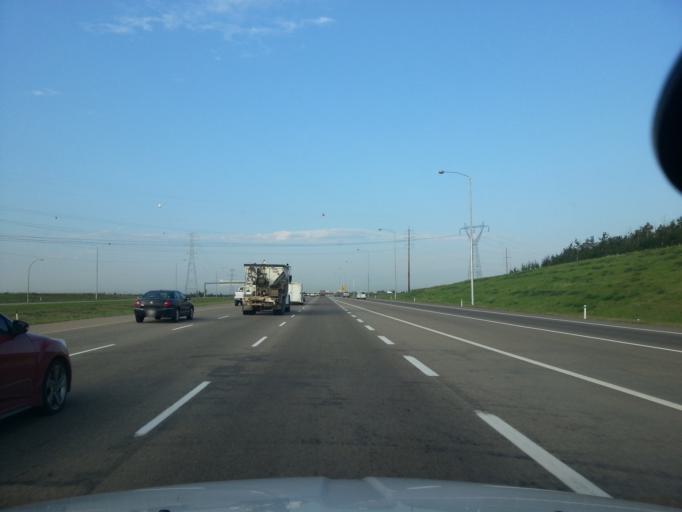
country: CA
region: Alberta
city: St. Albert
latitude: 53.6150
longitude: -113.6048
